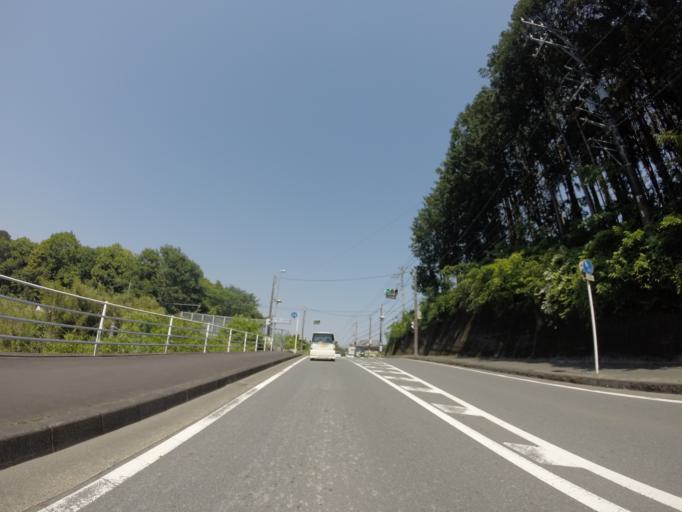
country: JP
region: Shizuoka
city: Fujinomiya
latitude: 35.2170
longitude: 138.5911
